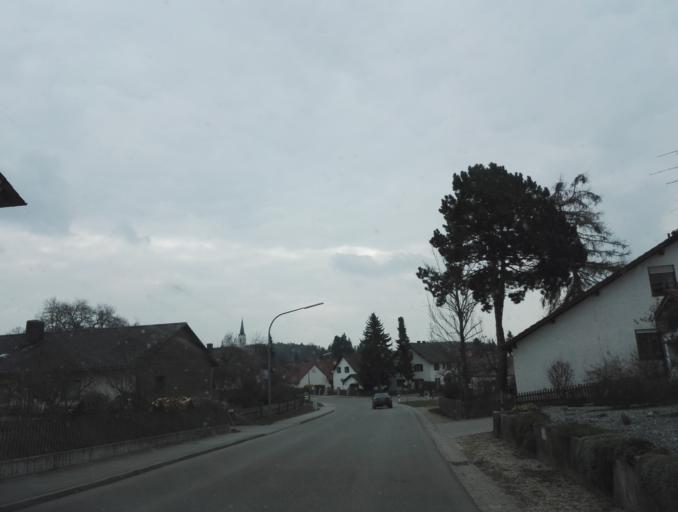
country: DE
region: Bavaria
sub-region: Lower Bavaria
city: Rottenburg an der Laaber
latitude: 48.6635
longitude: 12.0309
